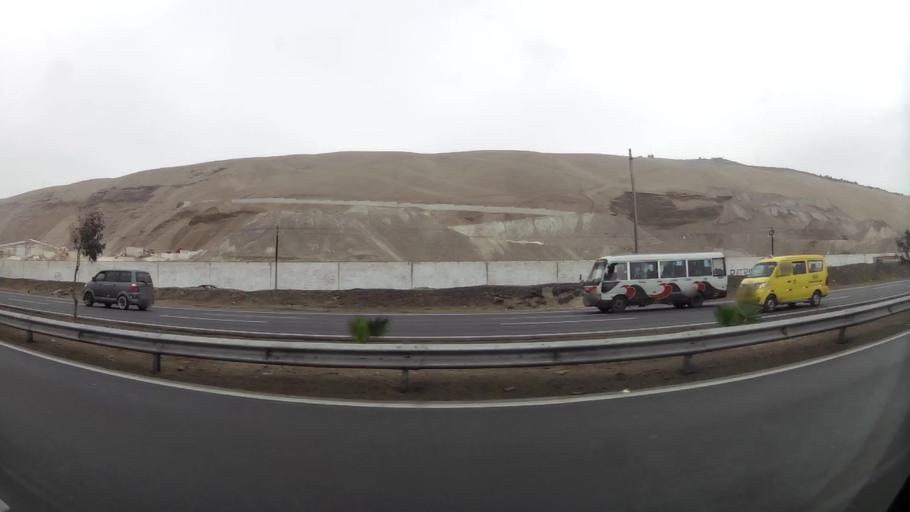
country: PE
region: Lima
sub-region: Lima
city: Surco
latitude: -12.2401
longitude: -76.9486
